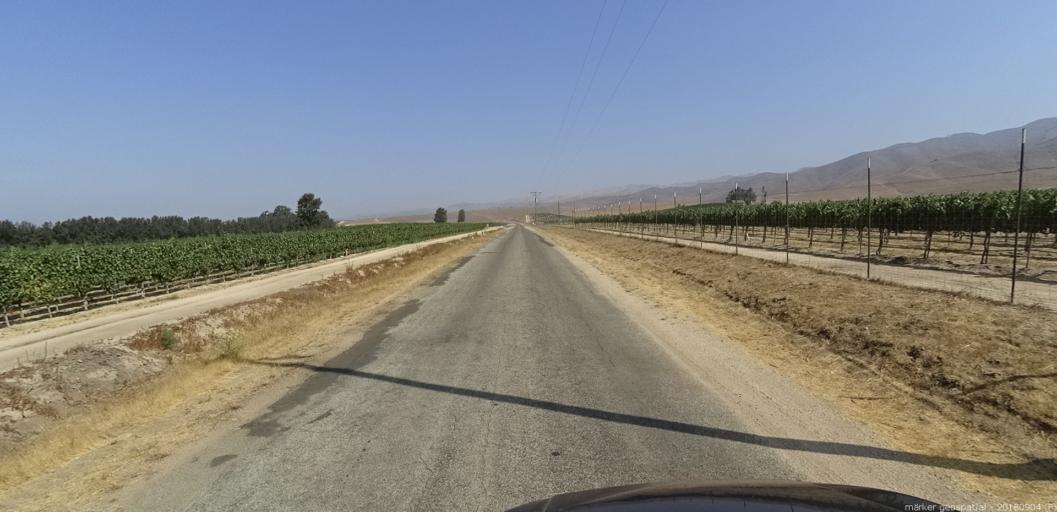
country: US
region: California
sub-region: Monterey County
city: Soledad
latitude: 36.4762
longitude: -121.3497
